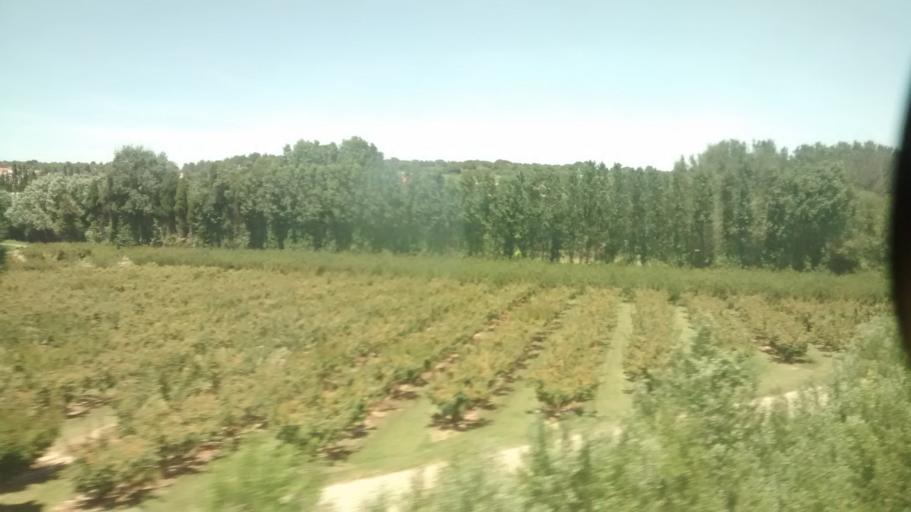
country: FR
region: Languedoc-Roussillon
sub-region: Departement du Gard
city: Montfrin
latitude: 43.8700
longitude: 4.6061
